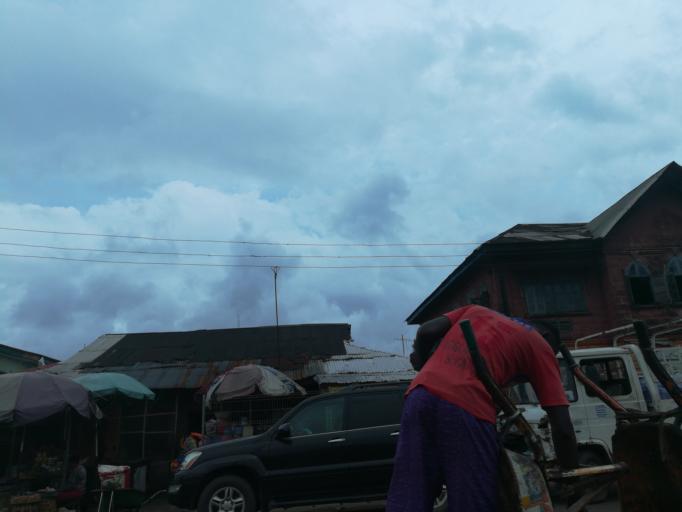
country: NG
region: Rivers
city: Port Harcourt
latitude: 4.7589
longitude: 7.0274
